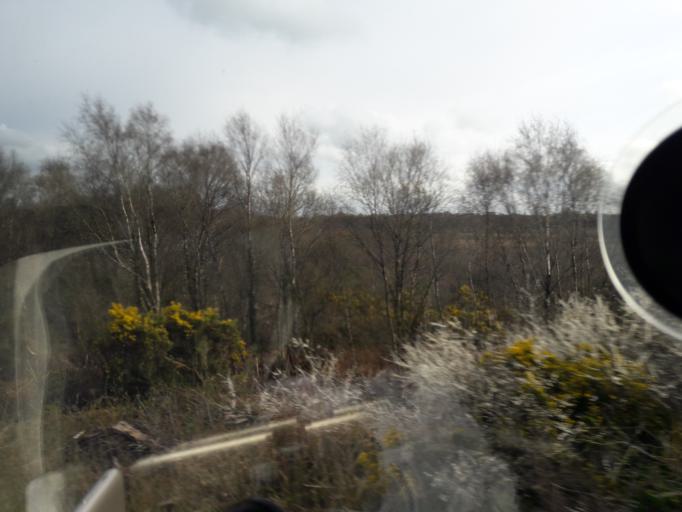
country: IE
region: Leinster
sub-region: An Mhi
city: Ballivor
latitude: 53.4710
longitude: -6.9913
